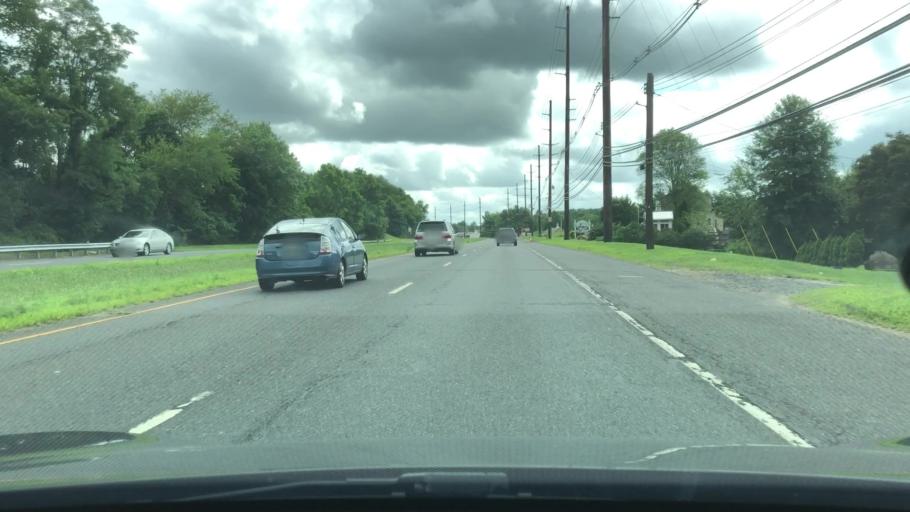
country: US
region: New Jersey
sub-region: Mercer County
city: Twin Rivers
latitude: 40.2624
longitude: -74.4433
